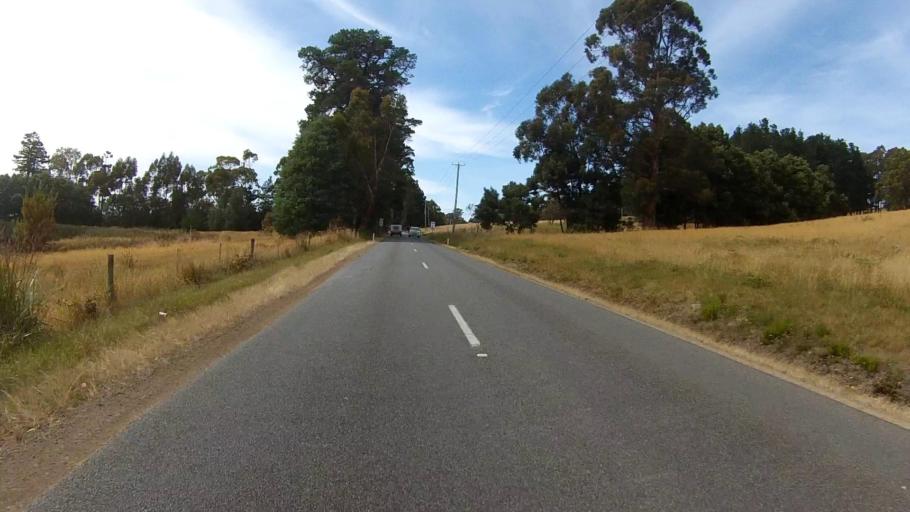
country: AU
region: Tasmania
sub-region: Kingborough
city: Kettering
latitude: -43.1938
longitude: 147.2481
